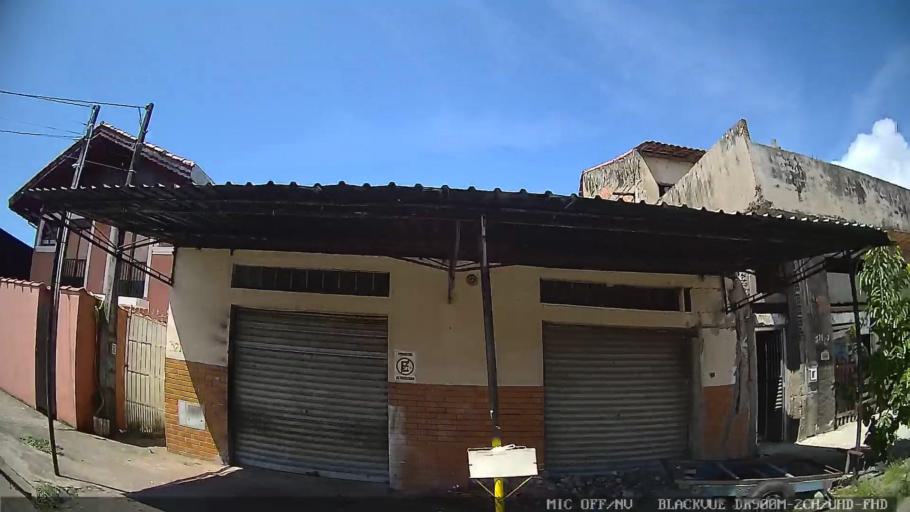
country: BR
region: Sao Paulo
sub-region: Peruibe
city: Peruibe
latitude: -24.3219
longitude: -47.0072
